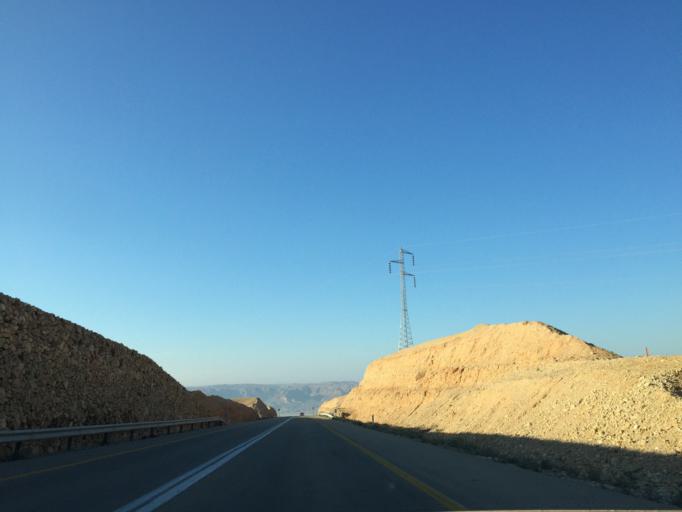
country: IL
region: Southern District
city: Mitzpe Ramon
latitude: 30.3527
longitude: 34.9594
